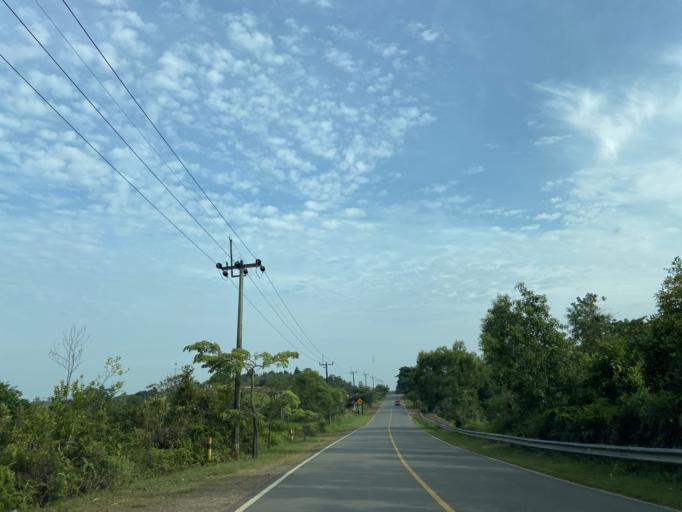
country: ID
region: Riau Islands
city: Tanjungpinang
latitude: 0.9068
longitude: 104.1242
